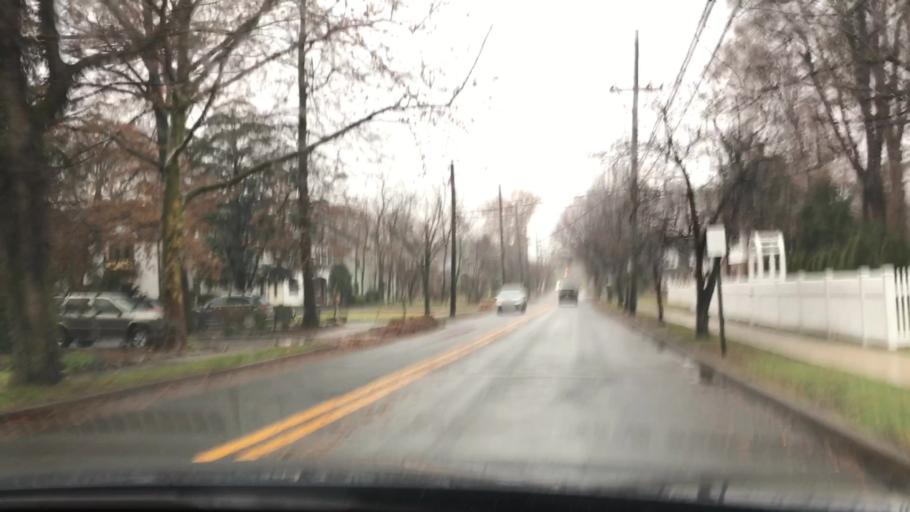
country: US
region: New Jersey
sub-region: Bergen County
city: Ho-Ho-Kus
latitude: 40.9814
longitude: -74.0982
